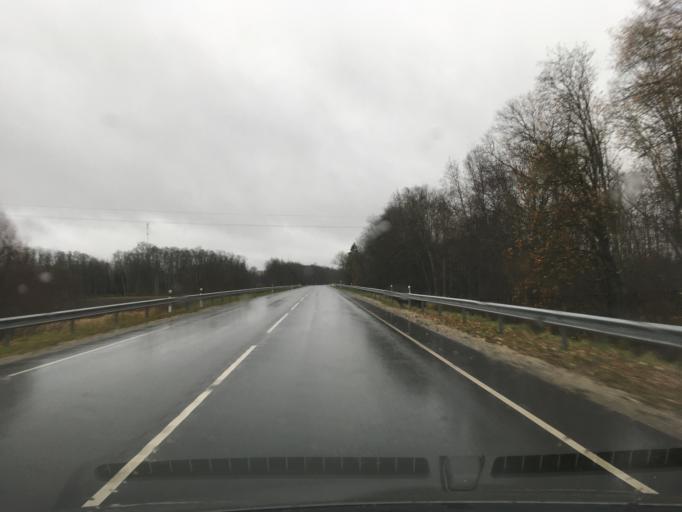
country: EE
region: Laeaene
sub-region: Lihula vald
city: Lihula
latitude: 58.8260
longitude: 24.0560
